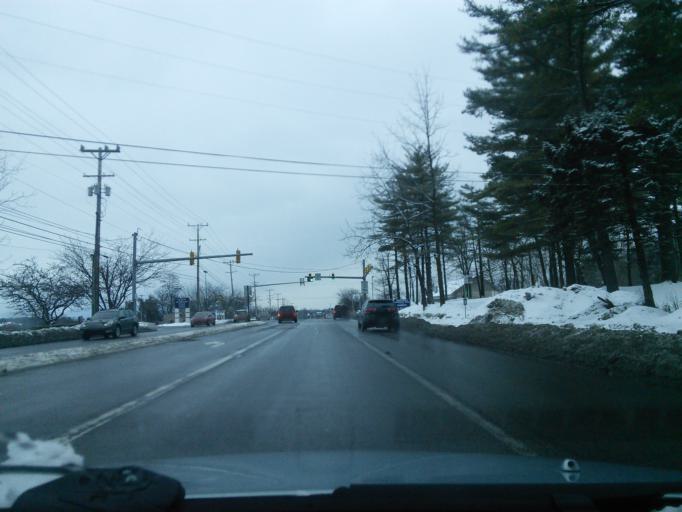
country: US
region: Pennsylvania
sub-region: Centre County
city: Park Forest Village
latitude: 40.8084
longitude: -77.8991
